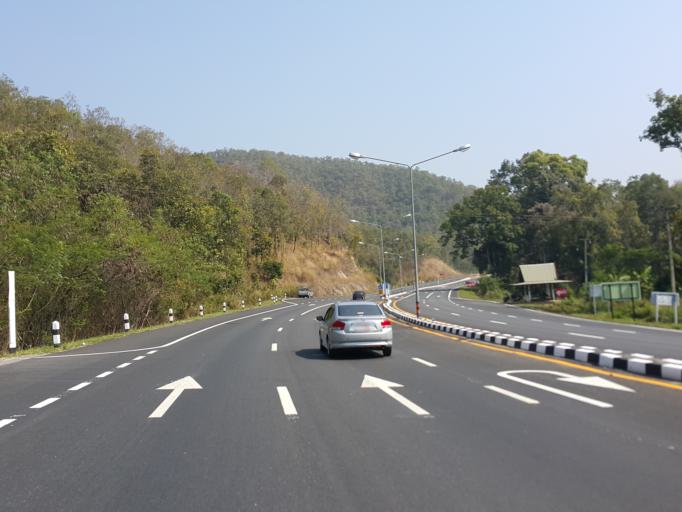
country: TH
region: Chiang Mai
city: San Sai
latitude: 18.8919
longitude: 99.1684
